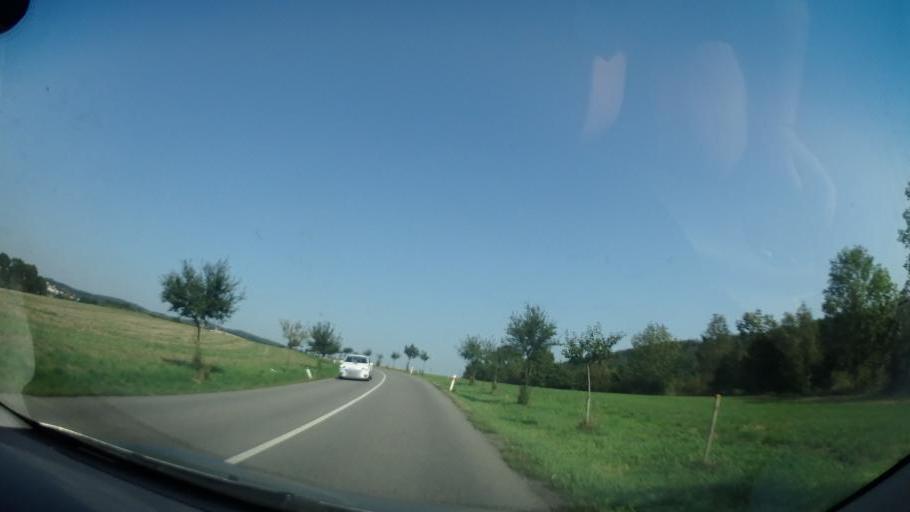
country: CZ
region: South Moravian
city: Kurim
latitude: 49.2455
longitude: 16.5298
